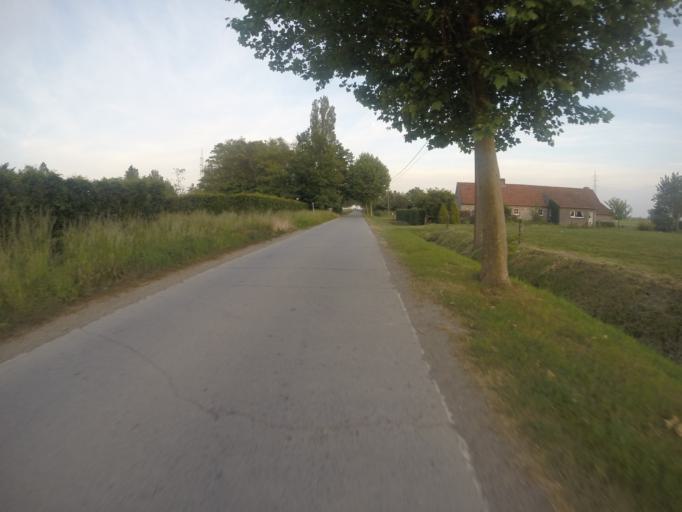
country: BE
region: Flanders
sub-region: Provincie Oost-Vlaanderen
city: Zomergem
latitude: 51.1246
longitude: 3.5277
